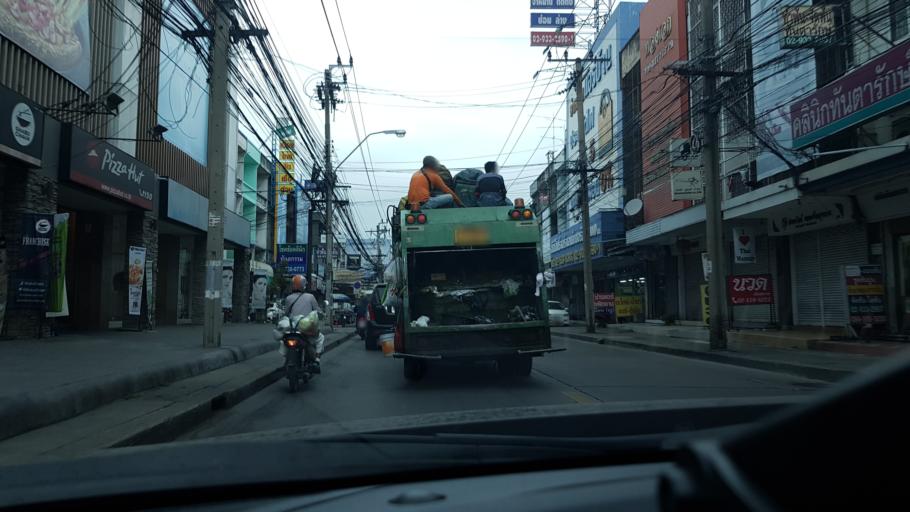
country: TH
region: Bangkok
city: Lat Phrao
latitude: 13.7979
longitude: 100.5957
